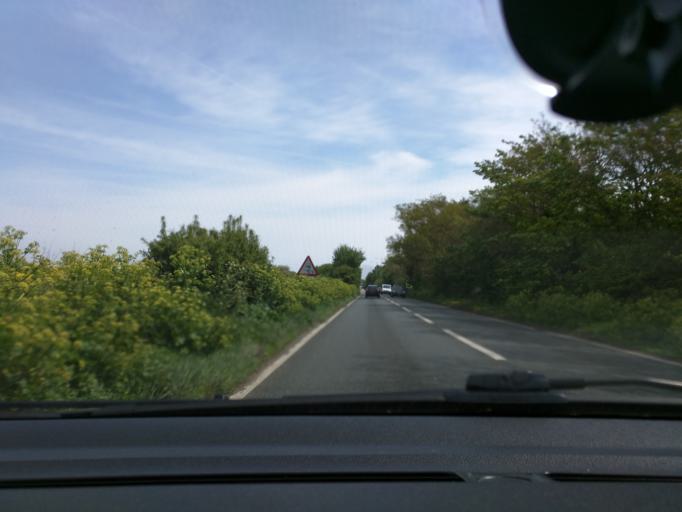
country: GB
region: England
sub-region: Suffolk
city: Kessingland
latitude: 52.4178
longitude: 1.6989
